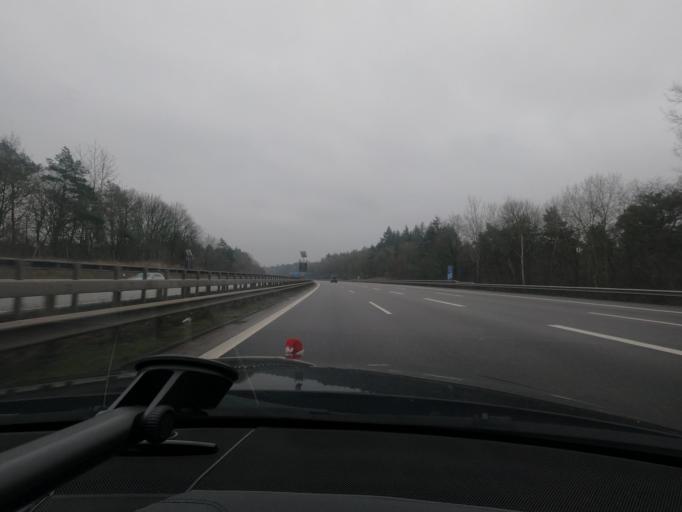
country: DE
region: Lower Saxony
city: Seevetal
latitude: 53.4437
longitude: 9.9190
